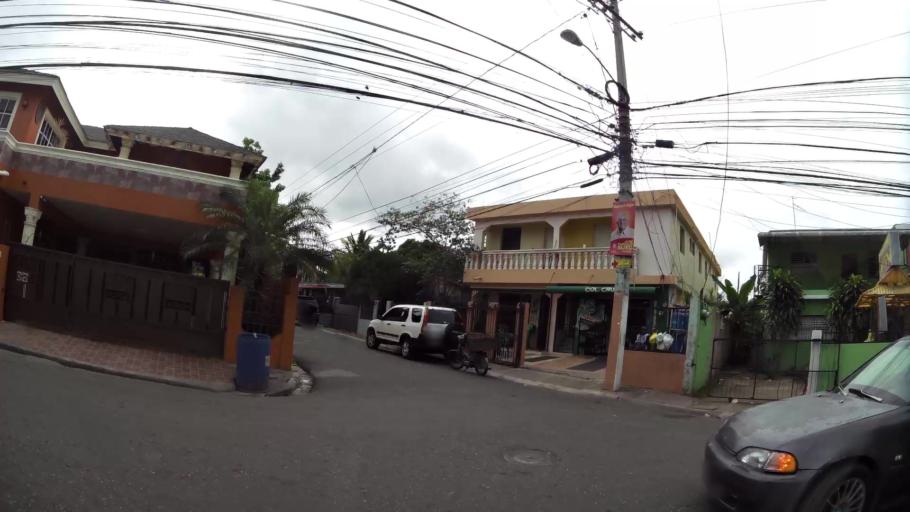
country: DO
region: Santiago
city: Santiago de los Caballeros
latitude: 19.4605
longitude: -70.6680
